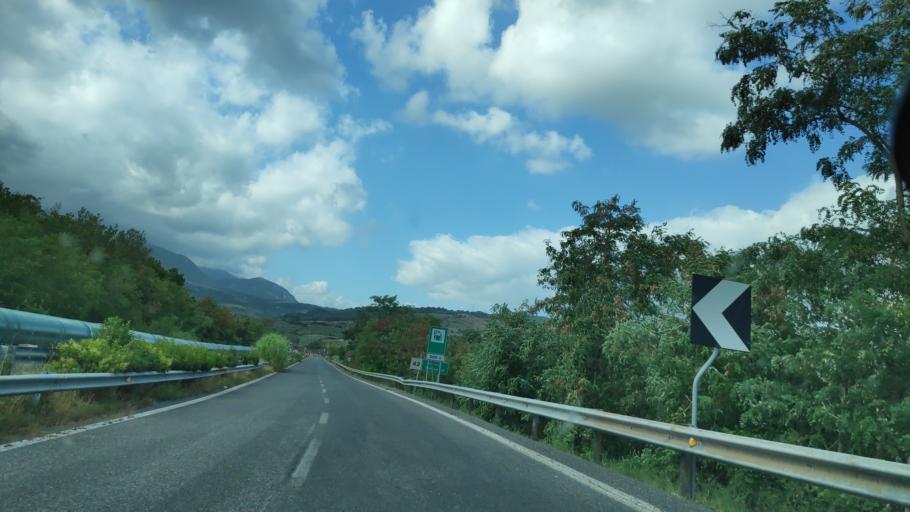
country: IT
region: Campania
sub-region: Provincia di Salerno
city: Serre
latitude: 40.6184
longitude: 15.1811
